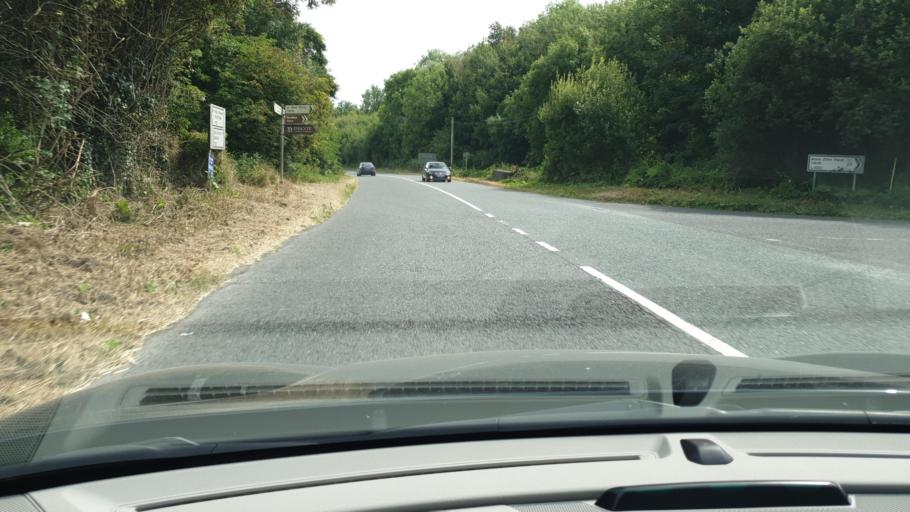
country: IE
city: Kentstown
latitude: 53.6234
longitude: -6.5188
